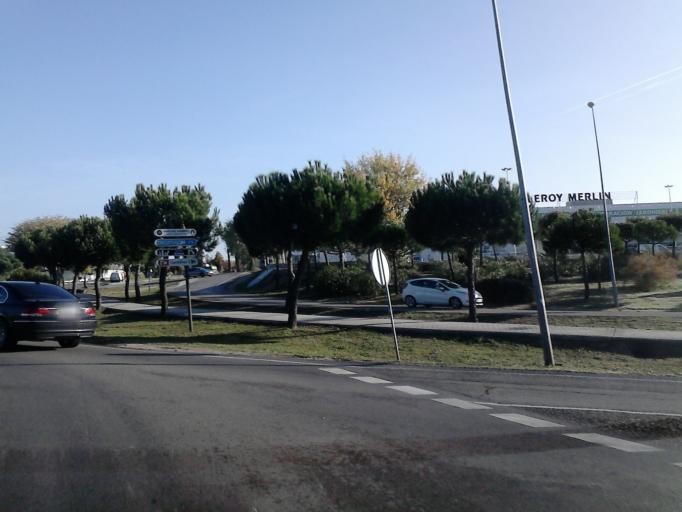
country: ES
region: Madrid
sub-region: Provincia de Madrid
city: Majadahonda
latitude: 40.4567
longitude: -3.8763
